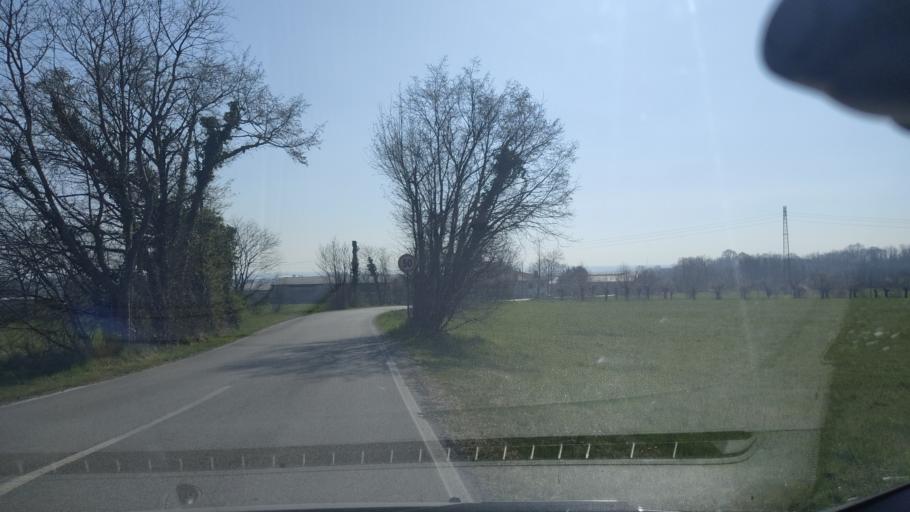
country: IT
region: Friuli Venezia Giulia
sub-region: Provincia di Pordenone
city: Budoia
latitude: 46.0528
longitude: 12.5424
